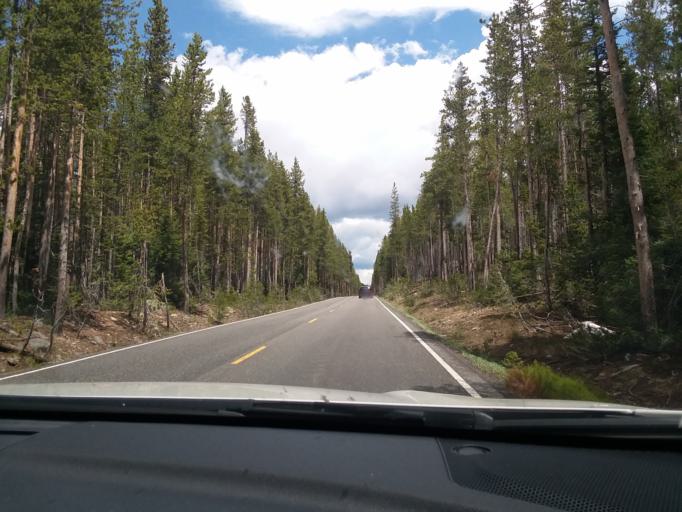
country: US
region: Idaho
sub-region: Teton County
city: Driggs
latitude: 44.1784
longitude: -110.6604
